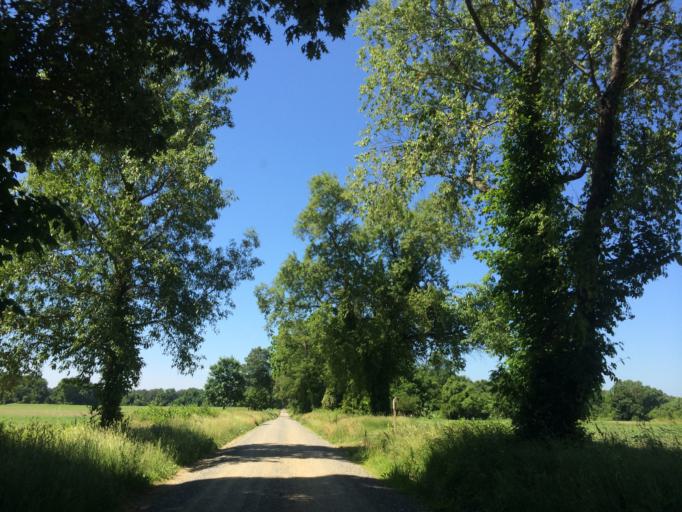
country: US
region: Maryland
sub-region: Queen Anne's County
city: Grasonville
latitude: 38.8925
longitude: -76.1576
